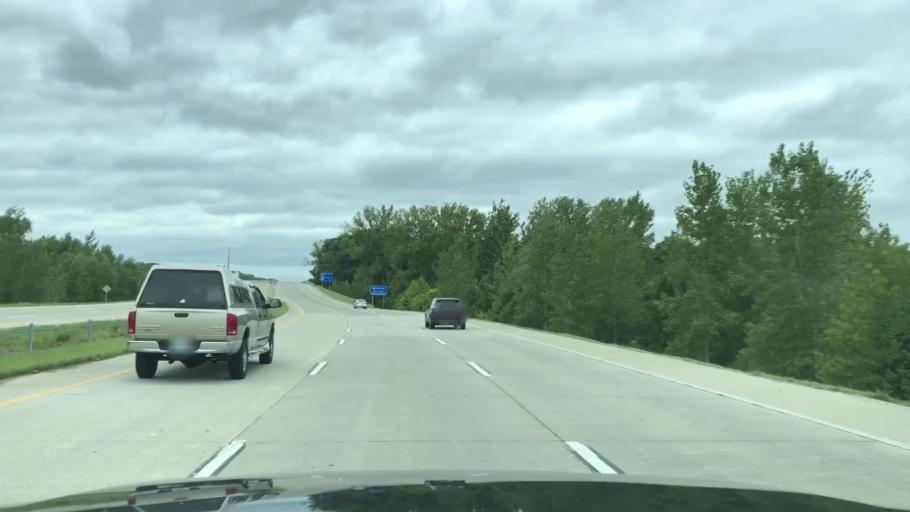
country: US
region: Missouri
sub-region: Saint Louis County
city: Maryland Heights
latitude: 38.6961
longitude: -90.5024
